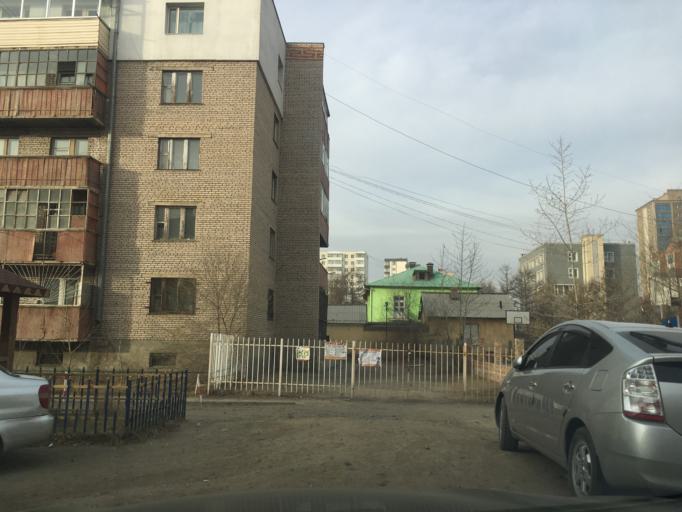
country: MN
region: Ulaanbaatar
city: Ulaanbaatar
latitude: 47.9159
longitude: 106.8793
